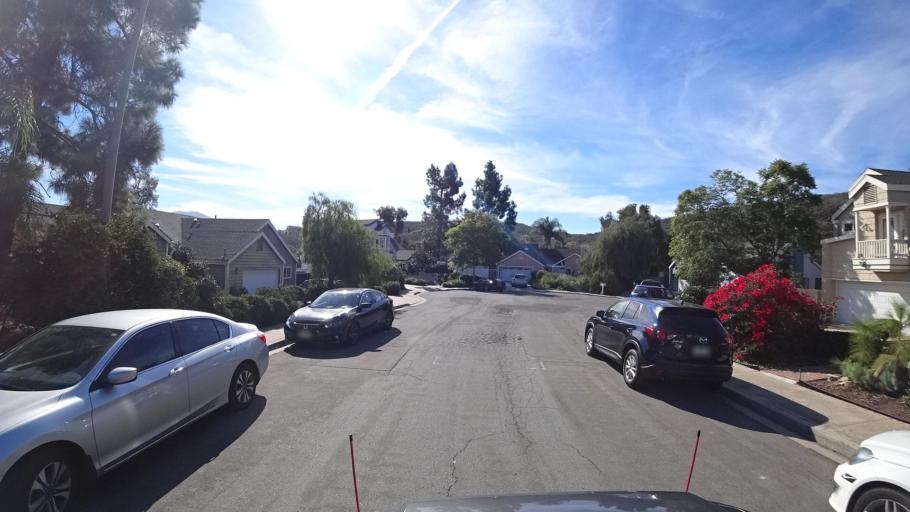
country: US
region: California
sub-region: San Diego County
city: Spring Valley
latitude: 32.7281
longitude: -116.9874
